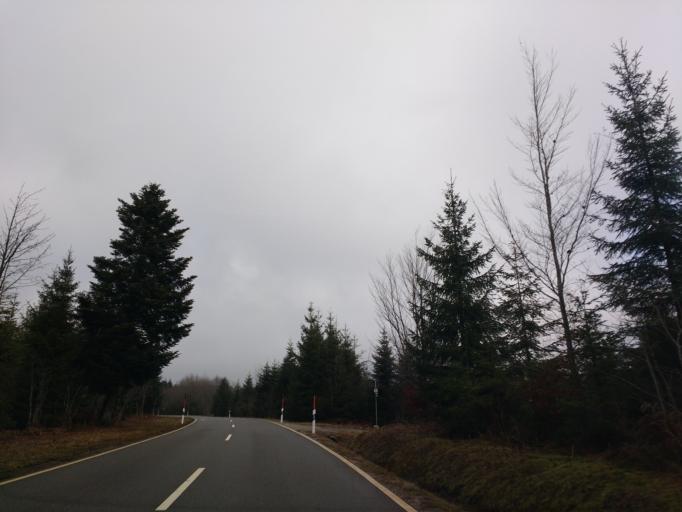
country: DE
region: Baden-Wuerttemberg
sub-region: Karlsruhe Region
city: Bad Rippoldsau-Schapbach
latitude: 48.4605
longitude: 8.2984
